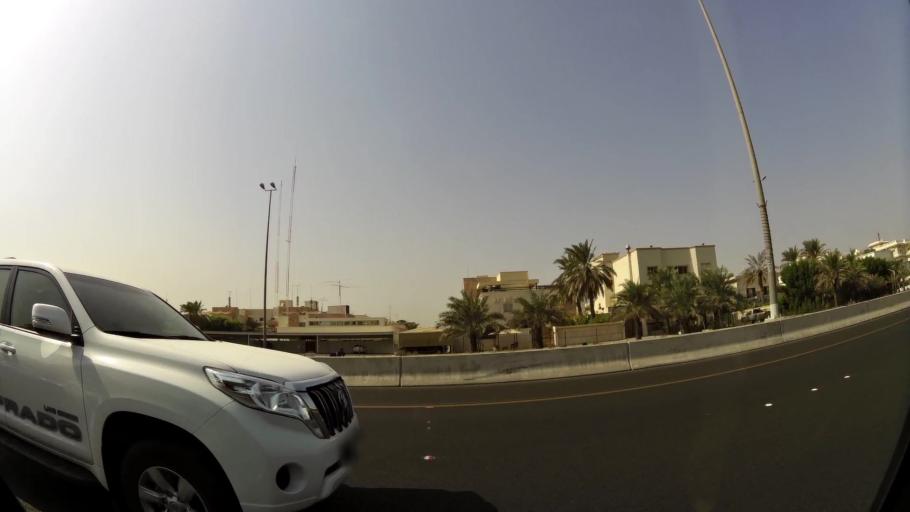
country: KW
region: Al Asimah
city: Ad Dasmah
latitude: 29.3463
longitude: 47.9971
